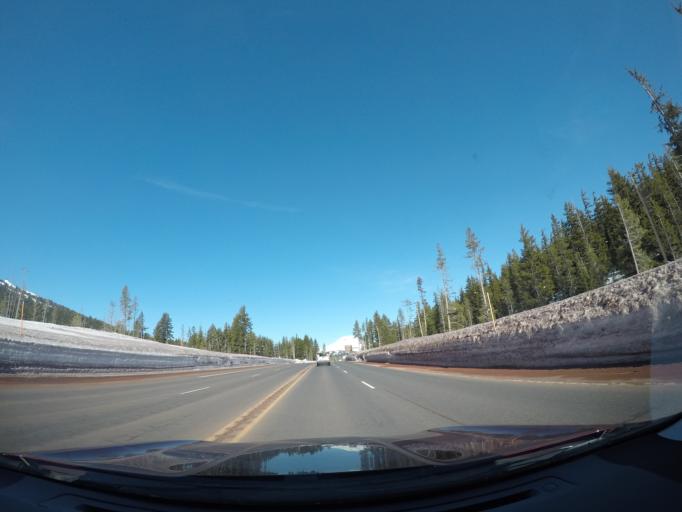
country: US
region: Oregon
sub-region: Deschutes County
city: Sunriver
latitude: 43.9939
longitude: -121.6587
